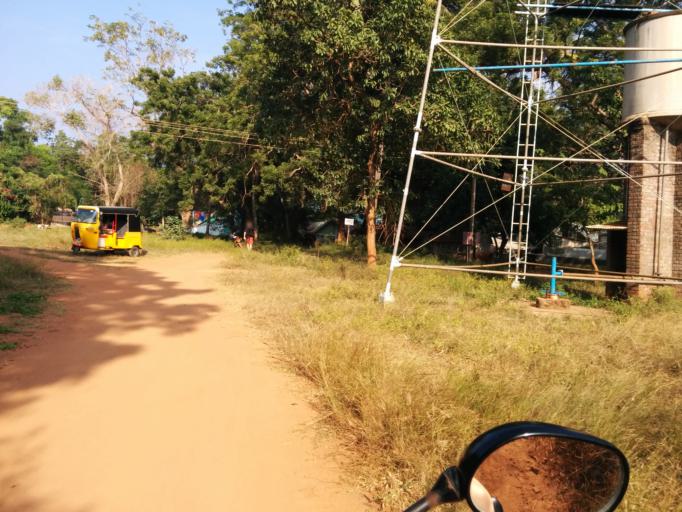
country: IN
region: Tamil Nadu
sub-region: Villupuram
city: Auroville
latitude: 11.9836
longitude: 79.8339
